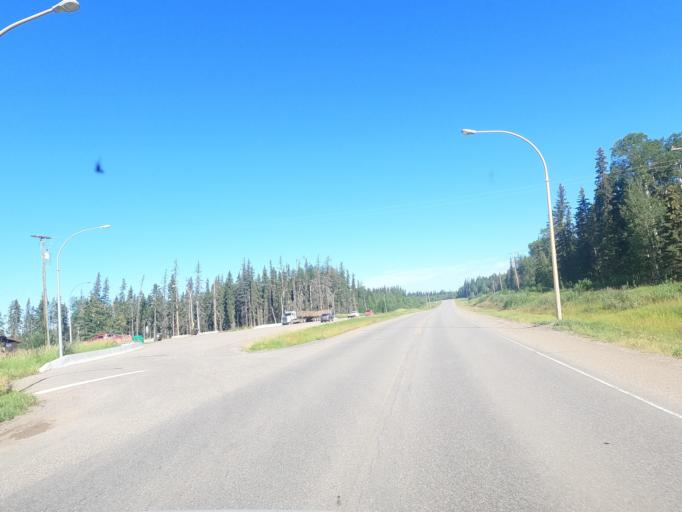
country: CA
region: British Columbia
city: Fort St. John
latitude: 56.5617
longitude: -121.3841
